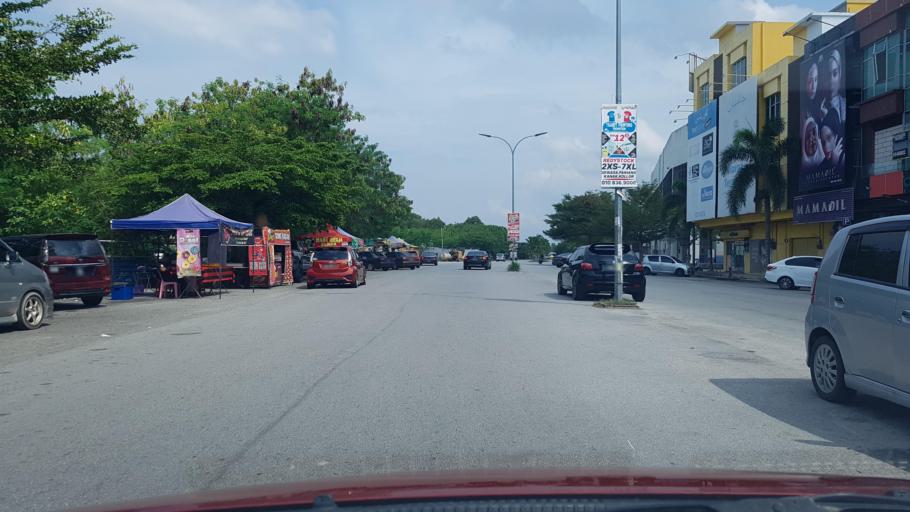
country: MY
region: Terengganu
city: Kuala Terengganu
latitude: 5.3570
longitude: 103.0968
